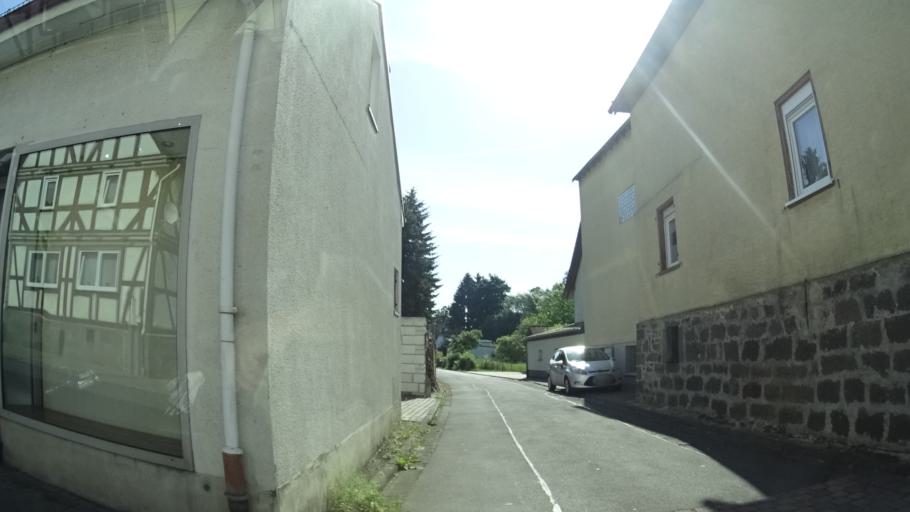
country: DE
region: Hesse
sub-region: Regierungsbezirk Giessen
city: Rabenau
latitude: 50.6771
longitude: 8.8228
